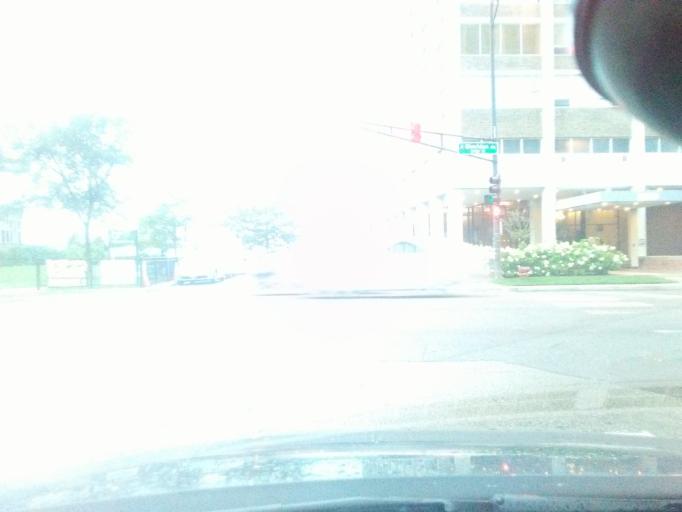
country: US
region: Illinois
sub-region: Cook County
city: Evanston
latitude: 41.9946
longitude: -87.6557
